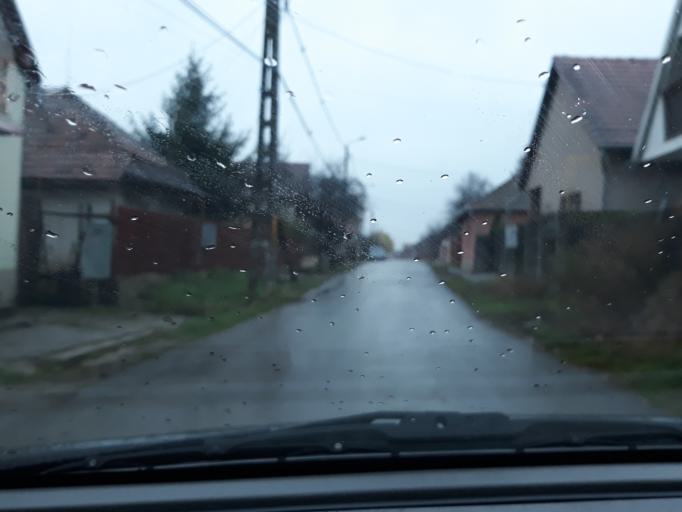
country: RO
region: Bihor
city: Margita
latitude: 47.3507
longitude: 22.3527
